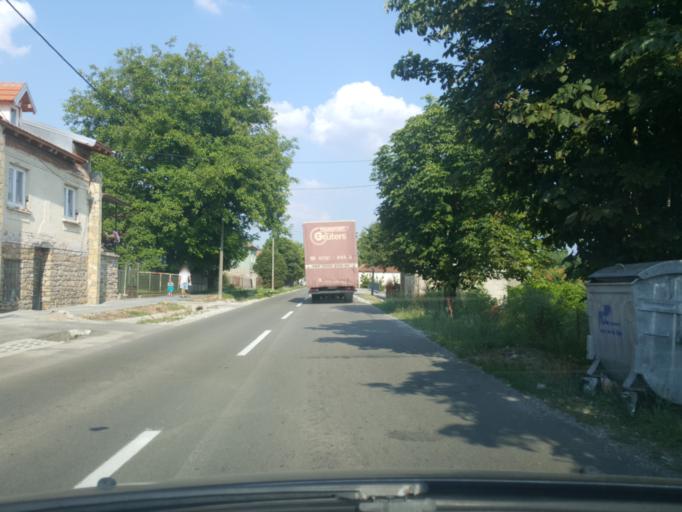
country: RS
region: Central Serbia
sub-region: Sumadijski Okrug
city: Topola
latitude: 44.1938
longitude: 20.6001
